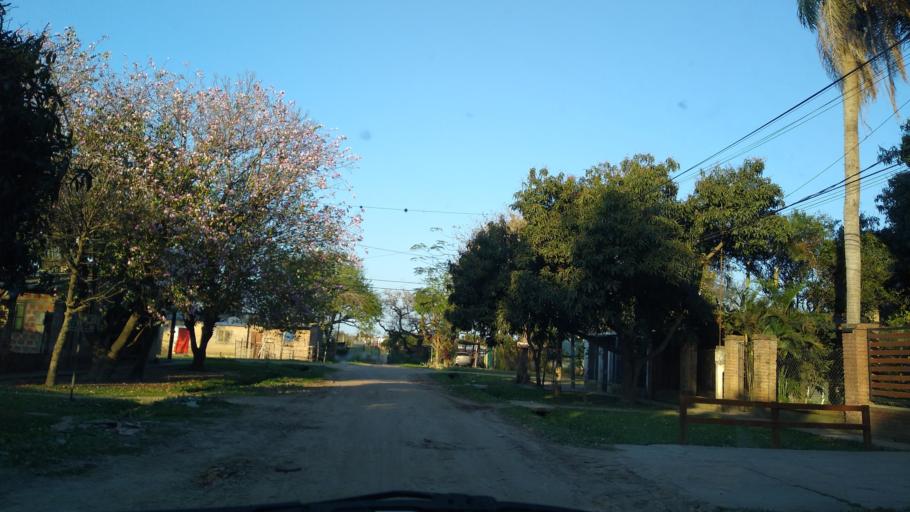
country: AR
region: Chaco
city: Barranqueras
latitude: -27.4715
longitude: -58.9559
